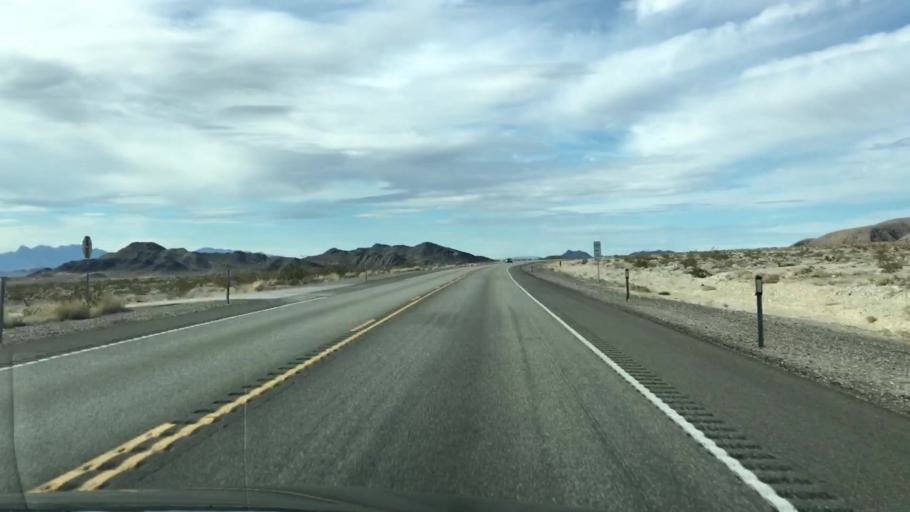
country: US
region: Nevada
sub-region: Nye County
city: Pahrump
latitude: 36.5728
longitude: -116.1800
